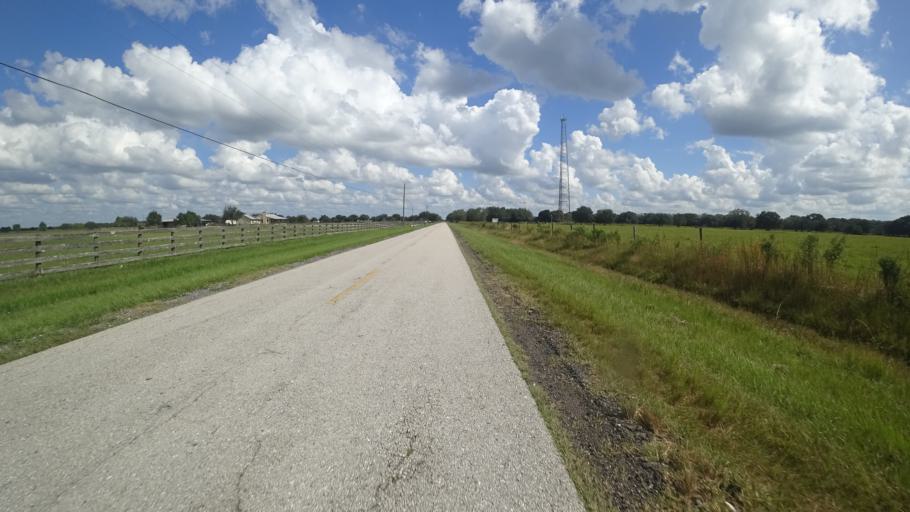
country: US
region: Florida
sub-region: Sarasota County
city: Warm Mineral Springs
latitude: 27.2738
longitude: -82.1842
